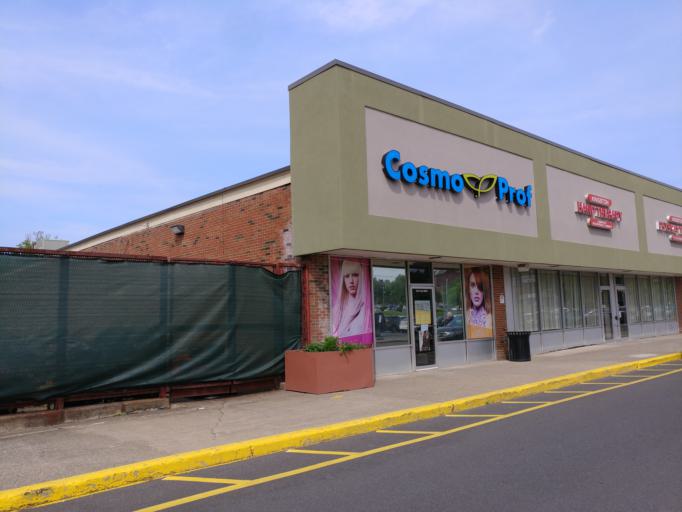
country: US
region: New York
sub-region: Ulster County
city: Kingston
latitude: 41.9374
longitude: -74.0214
